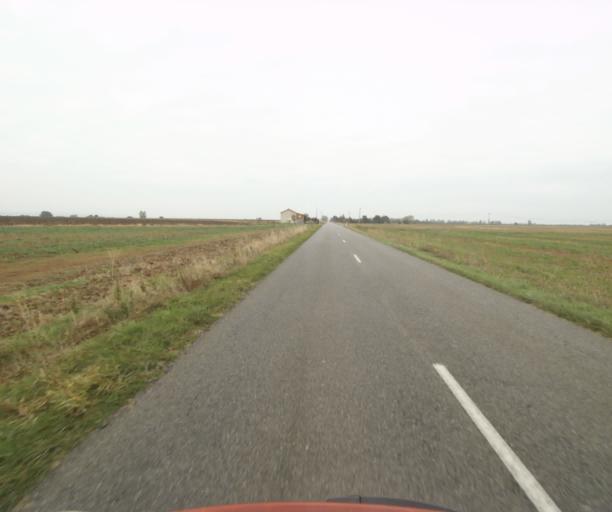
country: FR
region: Midi-Pyrenees
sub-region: Departement du Tarn-et-Garonne
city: Verdun-sur-Garonne
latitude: 43.8147
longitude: 1.1940
